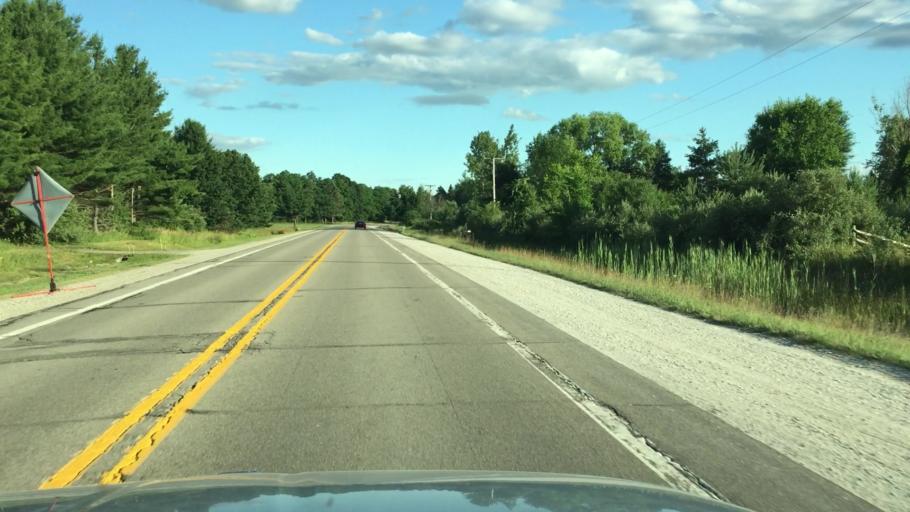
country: US
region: Michigan
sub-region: Saint Clair County
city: Yale
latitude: 43.0636
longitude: -82.7661
